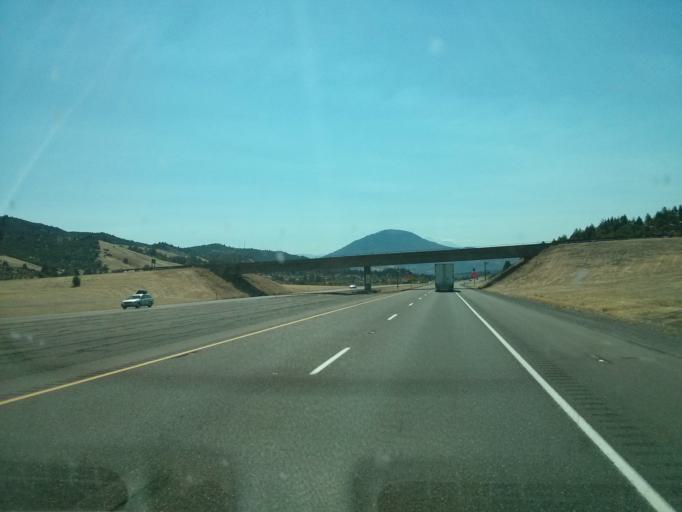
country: US
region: California
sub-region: Siskiyou County
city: Yreka
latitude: 41.9558
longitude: -122.5933
